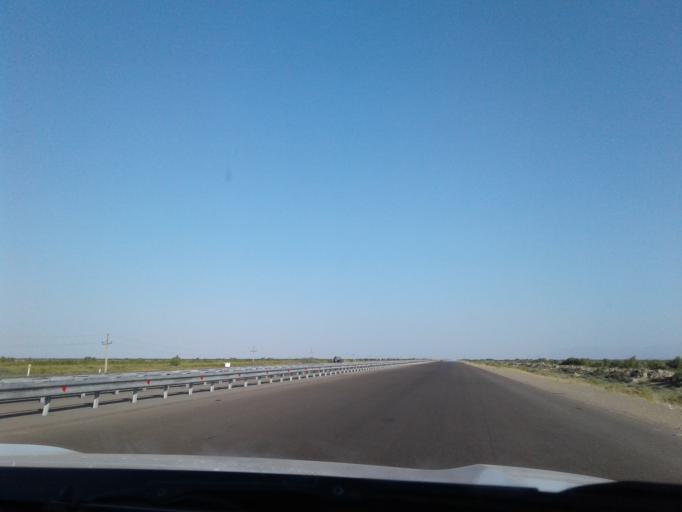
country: TM
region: Balkan
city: Serdar
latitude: 38.8872
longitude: 56.5388
